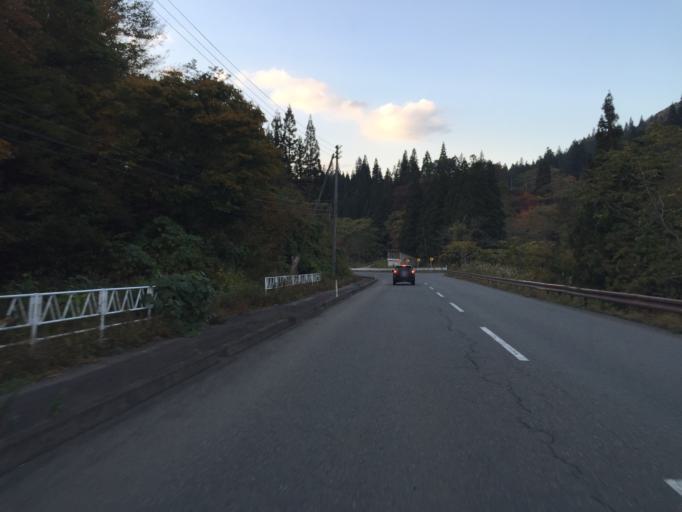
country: JP
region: Yamagata
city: Yonezawa
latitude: 37.8589
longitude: 139.9890
